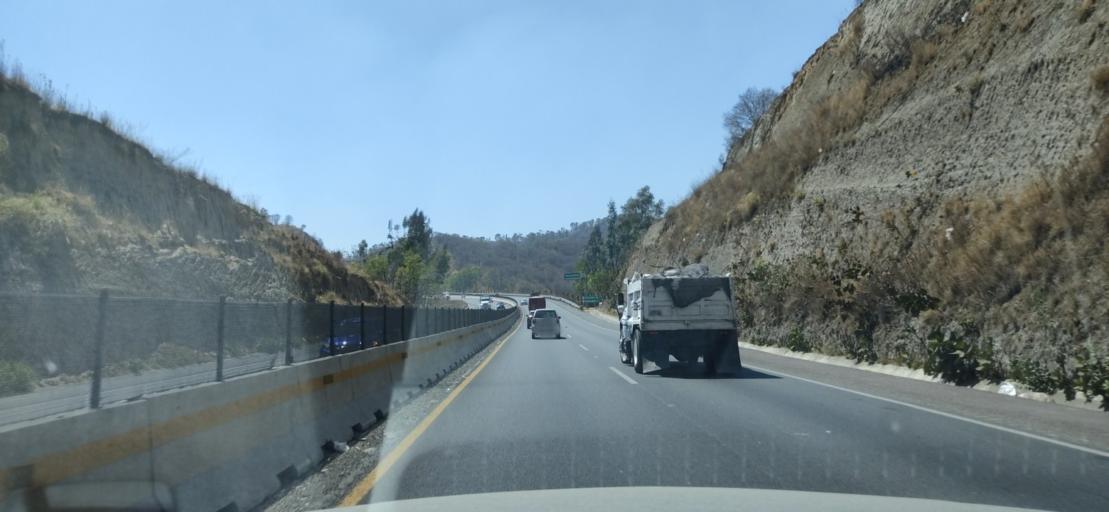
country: MX
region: Mexico
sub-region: Naucalpan de Juarez
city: La Rosa
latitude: 19.4829
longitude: -99.3130
